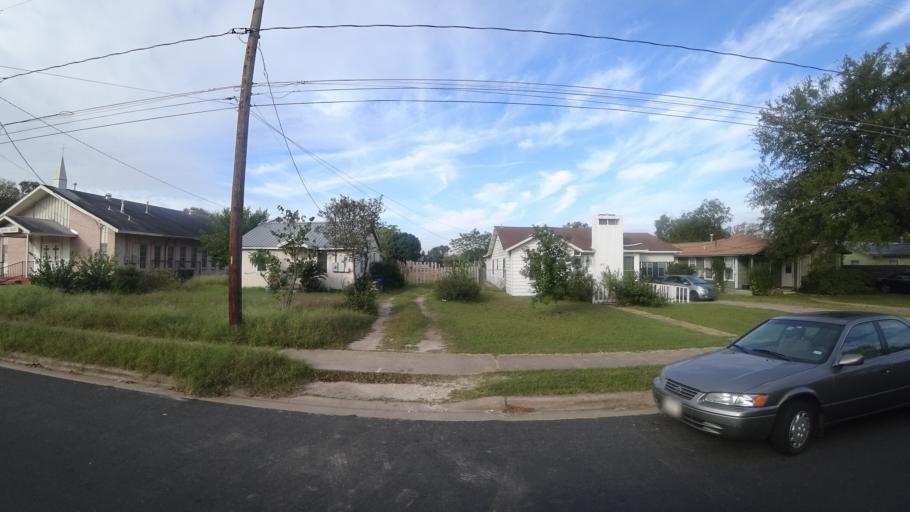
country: US
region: Texas
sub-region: Travis County
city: Austin
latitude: 30.2798
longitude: -97.7051
